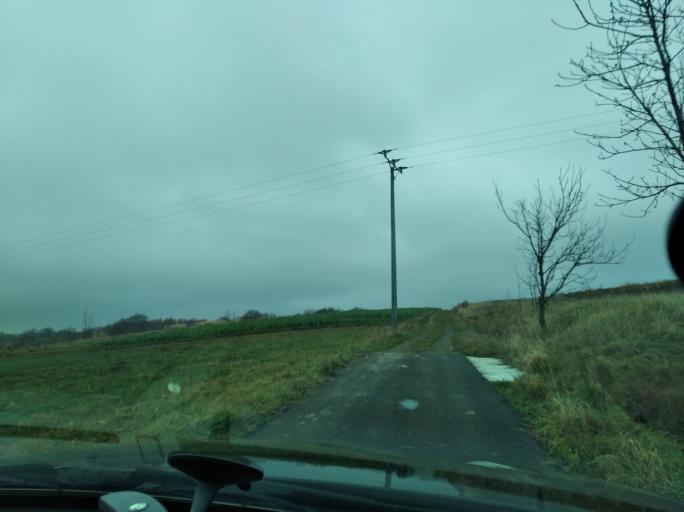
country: PL
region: Subcarpathian Voivodeship
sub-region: Powiat przeworski
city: Jawornik Polski
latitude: 49.8910
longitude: 22.2775
